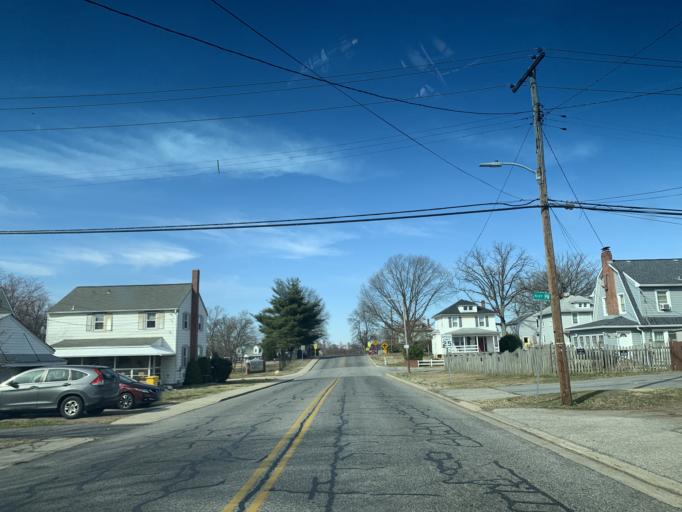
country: US
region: Maryland
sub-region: Anne Arundel County
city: Brooklyn Park
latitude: 39.2209
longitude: -76.6155
